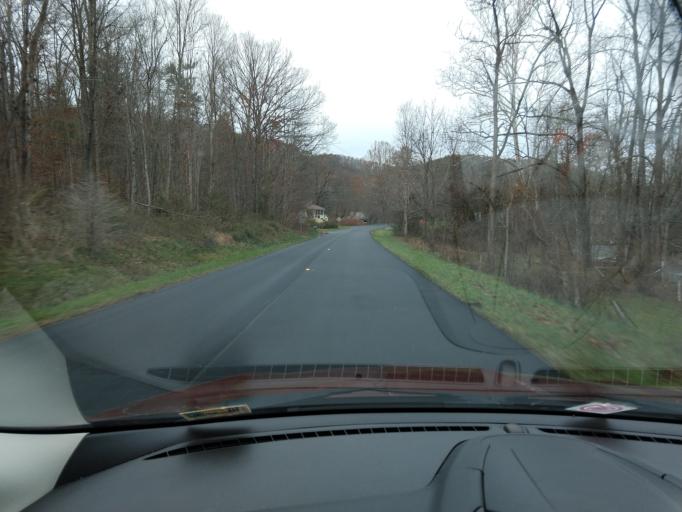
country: US
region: West Virginia
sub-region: Greenbrier County
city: White Sulphur Springs
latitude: 37.7226
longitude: -80.1988
